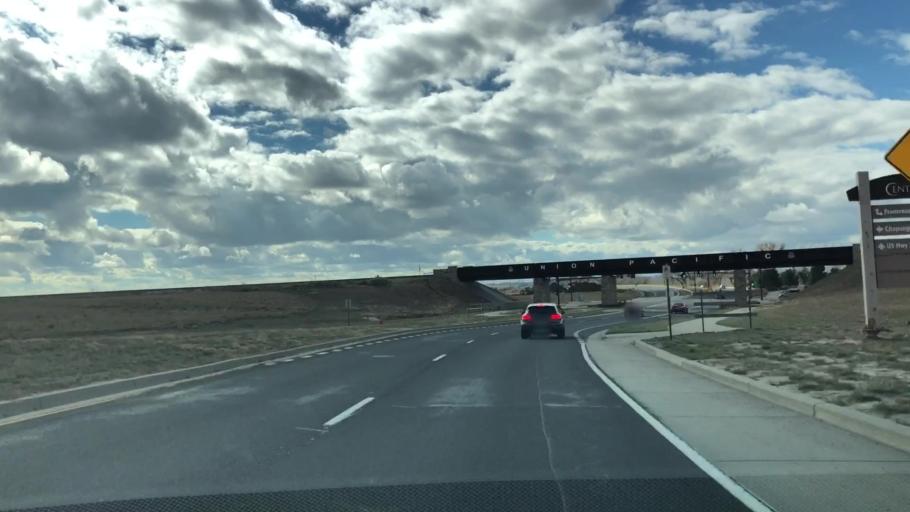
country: US
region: Colorado
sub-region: Larimer County
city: Loveland
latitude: 40.4177
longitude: -104.9838
